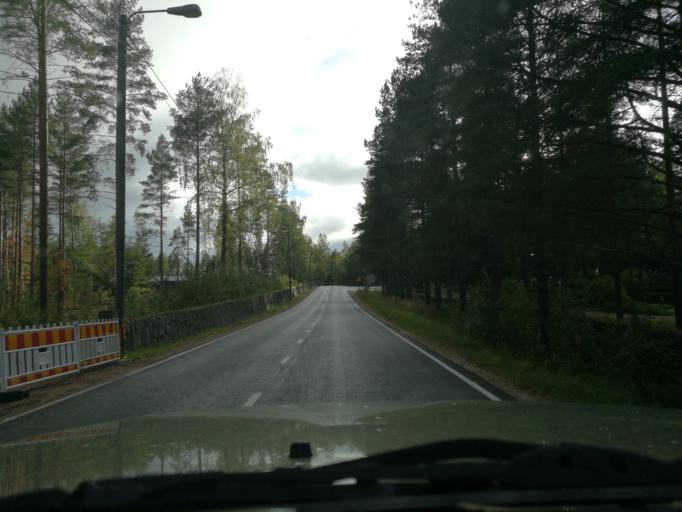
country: FI
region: Uusimaa
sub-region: Helsinki
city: Vantaa
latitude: 60.3170
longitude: 24.9961
